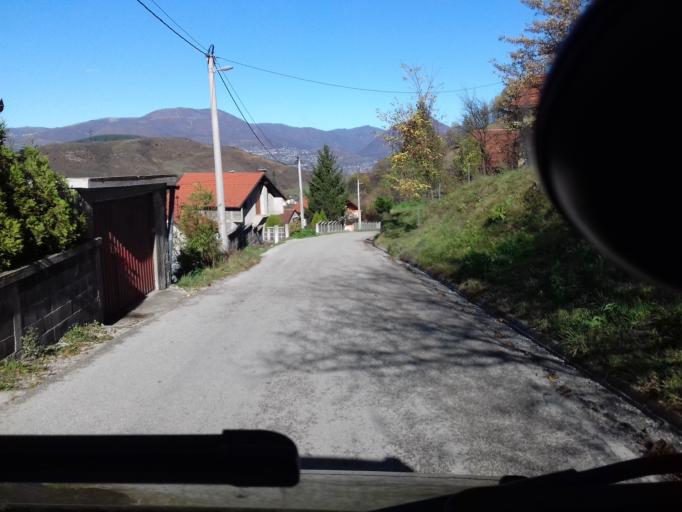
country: BA
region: Federation of Bosnia and Herzegovina
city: Zenica
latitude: 44.1776
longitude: 17.9063
